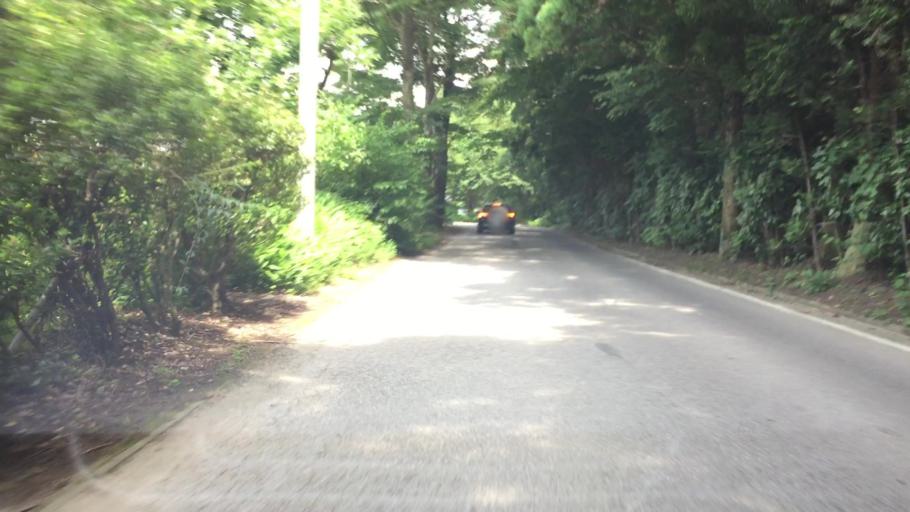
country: JP
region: Tochigi
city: Kuroiso
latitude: 37.0323
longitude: 139.9458
